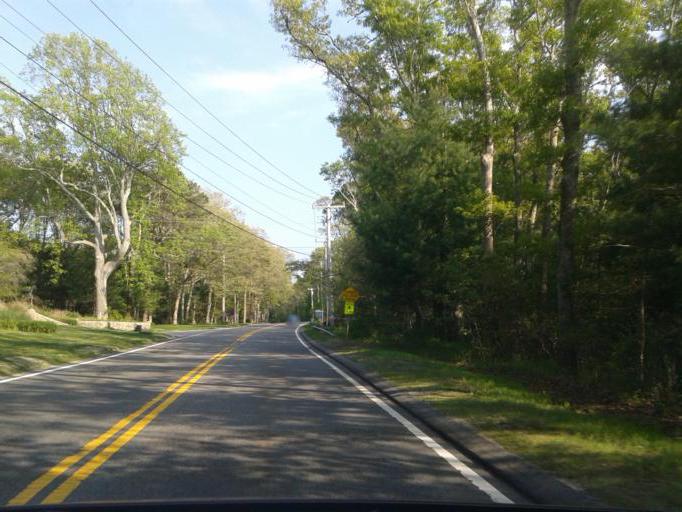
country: US
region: Massachusetts
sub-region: Barnstable County
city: West Falmouth
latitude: 41.5929
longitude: -70.6245
